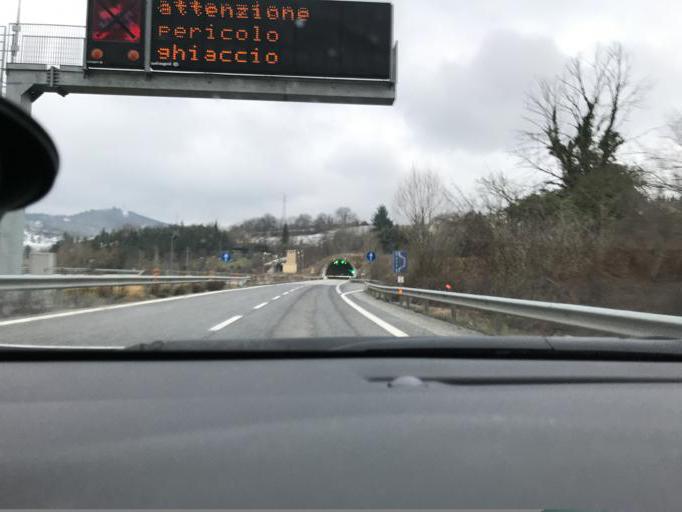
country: IT
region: The Marches
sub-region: Provincia di Ancona
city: Fabriano
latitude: 43.3268
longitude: 12.9200
